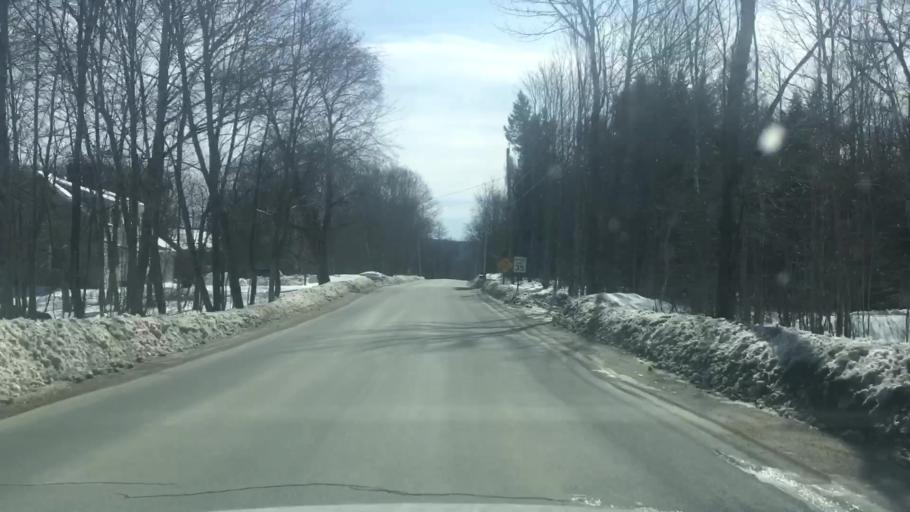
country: US
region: Maine
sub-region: Penobscot County
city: Holden
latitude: 44.7637
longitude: -68.6424
